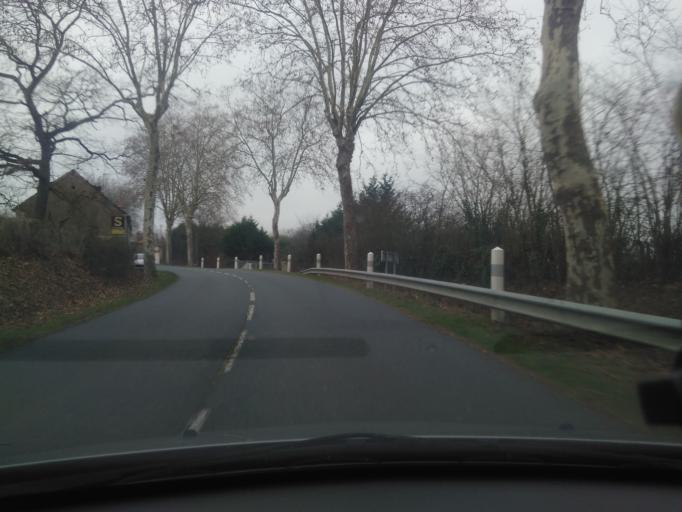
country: FR
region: Centre
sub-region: Departement du Cher
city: Le Chatelet
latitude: 46.6447
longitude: 2.2739
